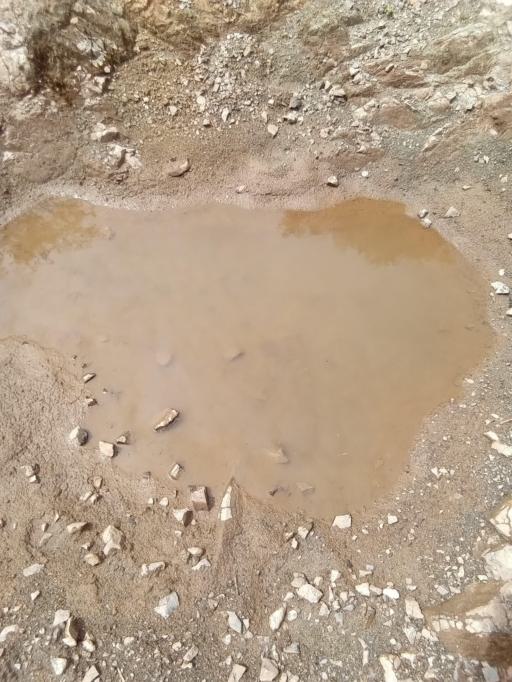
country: KE
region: Homa Bay
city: Homa Bay
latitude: -0.5113
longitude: 34.1663
